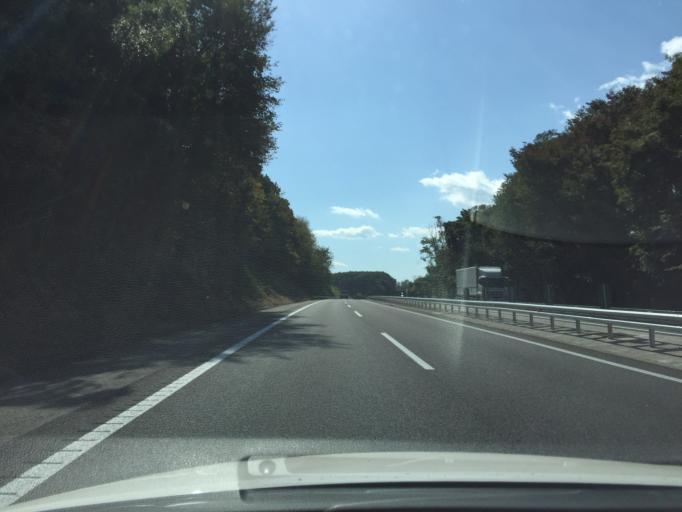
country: JP
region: Fukushima
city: Sukagawa
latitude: 37.2342
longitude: 140.3267
